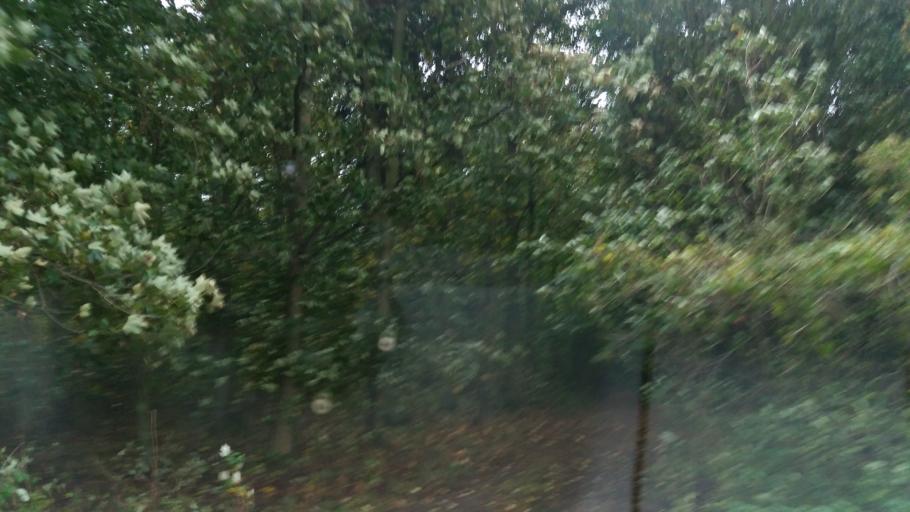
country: PL
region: West Pomeranian Voivodeship
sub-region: Powiat choszczenski
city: Pelczyce
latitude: 53.0702
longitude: 15.3011
